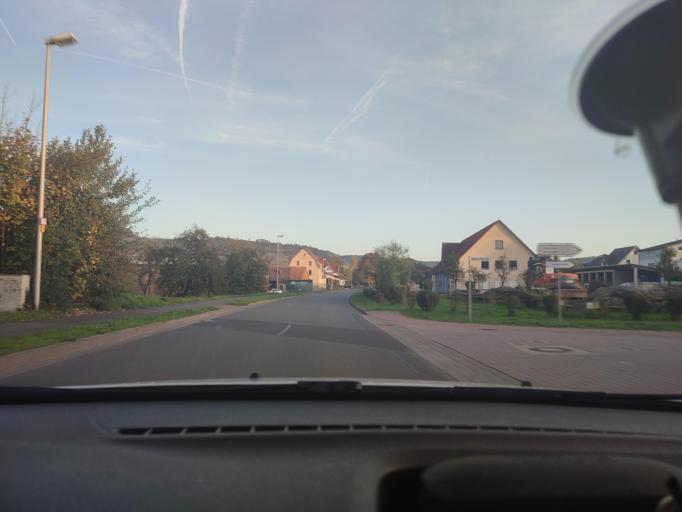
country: DE
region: Bavaria
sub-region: Regierungsbezirk Unterfranken
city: Marktheidenfeld
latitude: 49.8052
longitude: 9.6064
